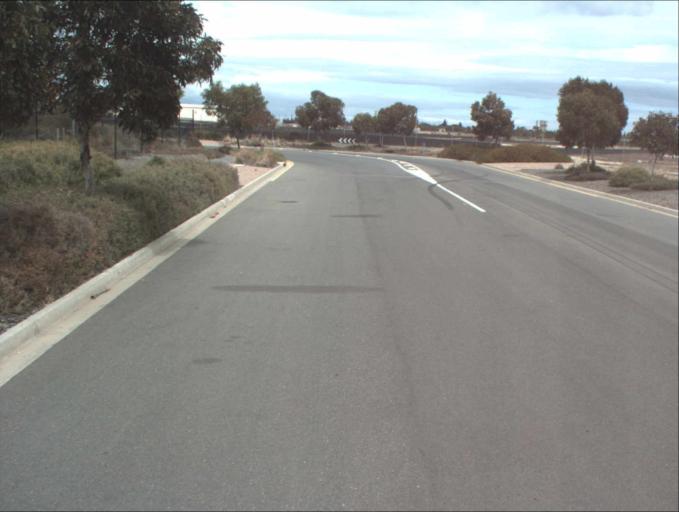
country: AU
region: South Australia
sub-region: Port Adelaide Enfield
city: Birkenhead
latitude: -34.7805
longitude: 138.5060
